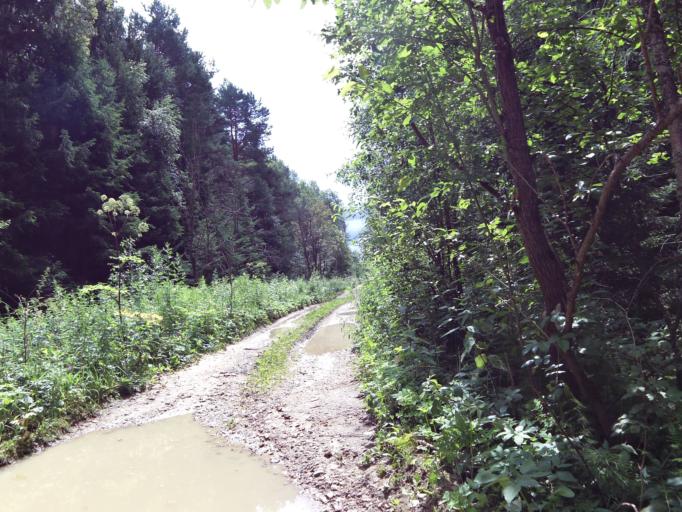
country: RU
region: Moskovskaya
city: Popovo
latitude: 54.9772
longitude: 37.6950
